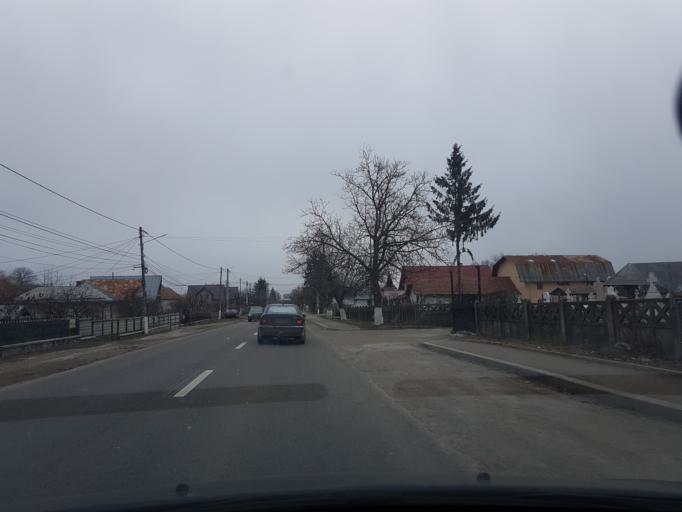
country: RO
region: Prahova
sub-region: Oras Breaza
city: Breaza de Jos
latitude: 45.1692
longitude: 25.6778
